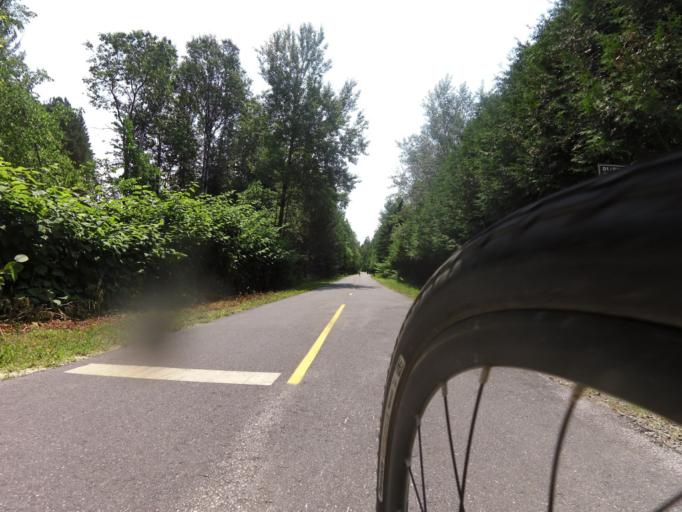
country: CA
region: Quebec
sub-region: Laurentides
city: Mont-Tremblant
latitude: 46.1376
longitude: -74.5966
